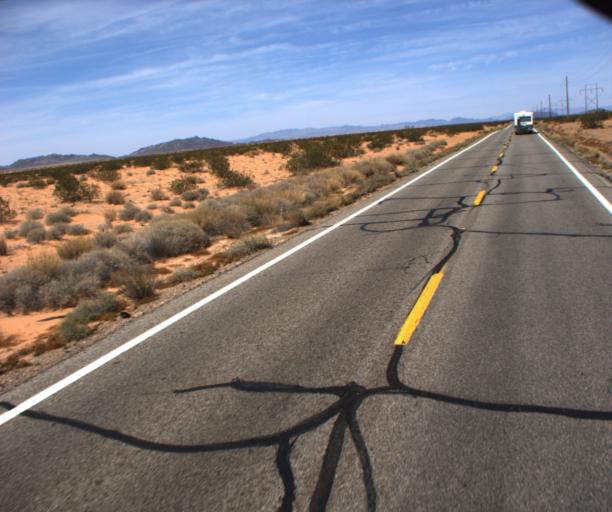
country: US
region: Arizona
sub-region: La Paz County
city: Quartzsite
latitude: 33.8923
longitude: -114.2169
